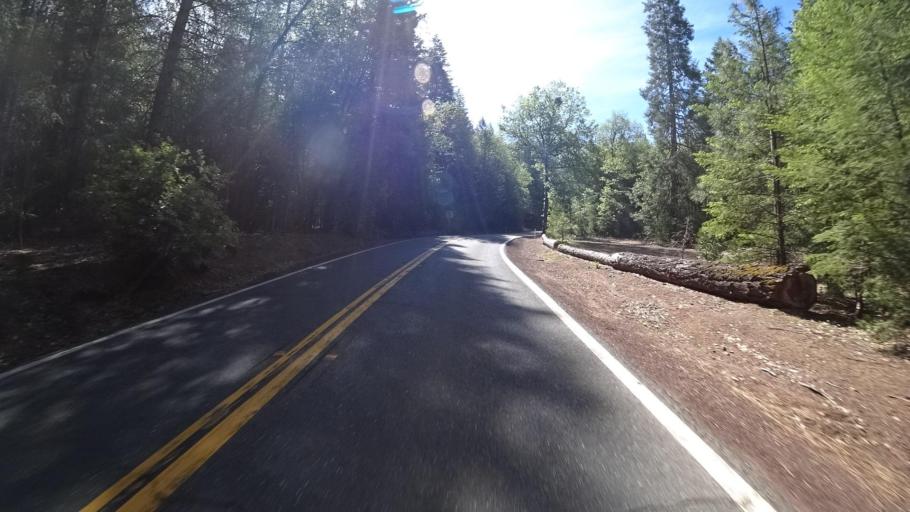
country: US
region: California
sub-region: Lake County
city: Cobb
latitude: 38.8698
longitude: -122.7197
